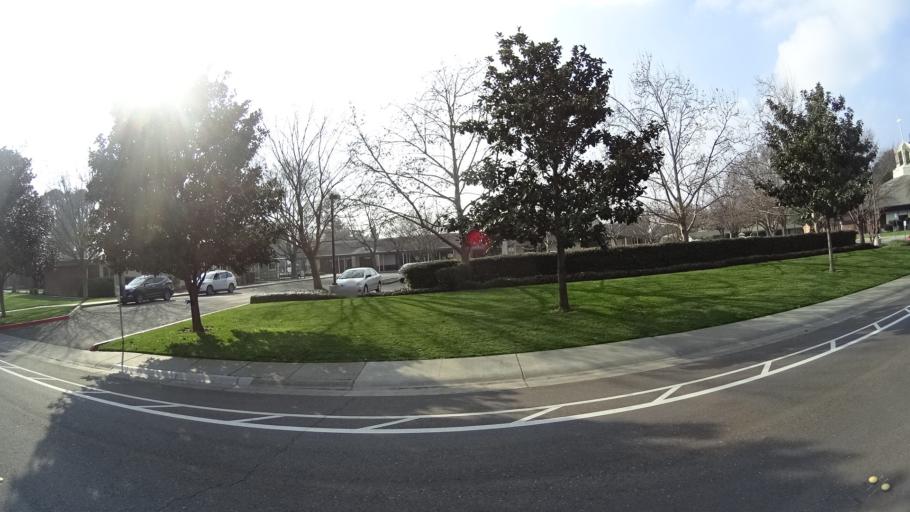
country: US
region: California
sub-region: Yolo County
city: Davis
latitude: 38.5549
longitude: -121.7471
